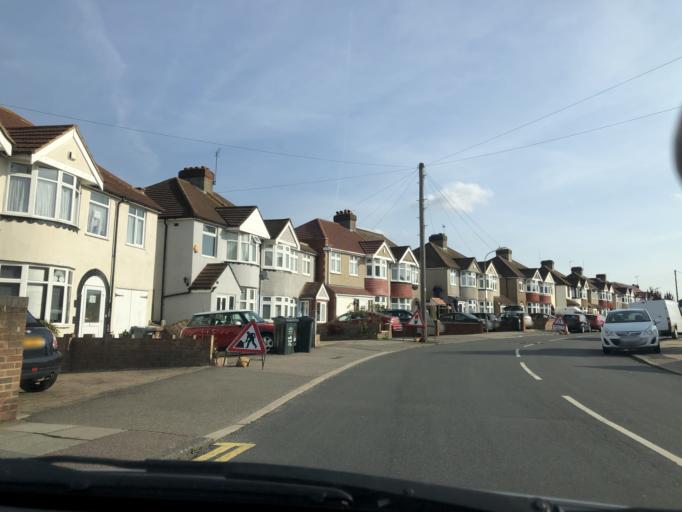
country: GB
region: England
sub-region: Kent
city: Dartford
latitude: 51.4440
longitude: 0.1856
